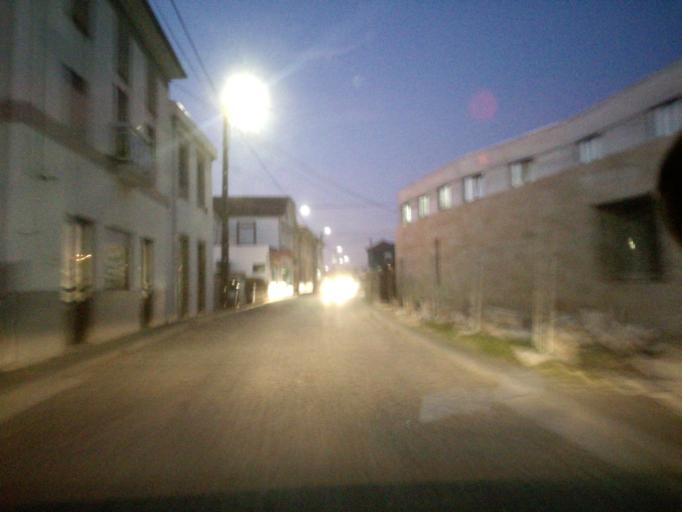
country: PT
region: Porto
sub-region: Maia
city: Nogueira
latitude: 41.2394
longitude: -8.5871
